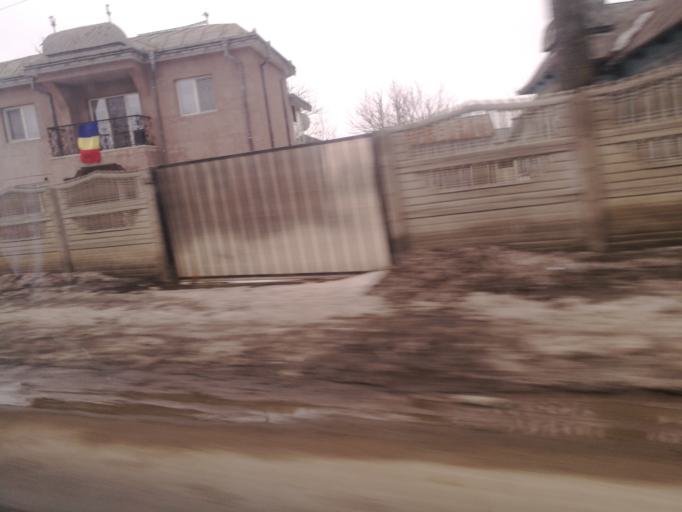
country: RO
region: Iasi
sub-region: Comuna Ruginoasa
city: Dumbravita
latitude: 47.2389
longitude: 26.8331
